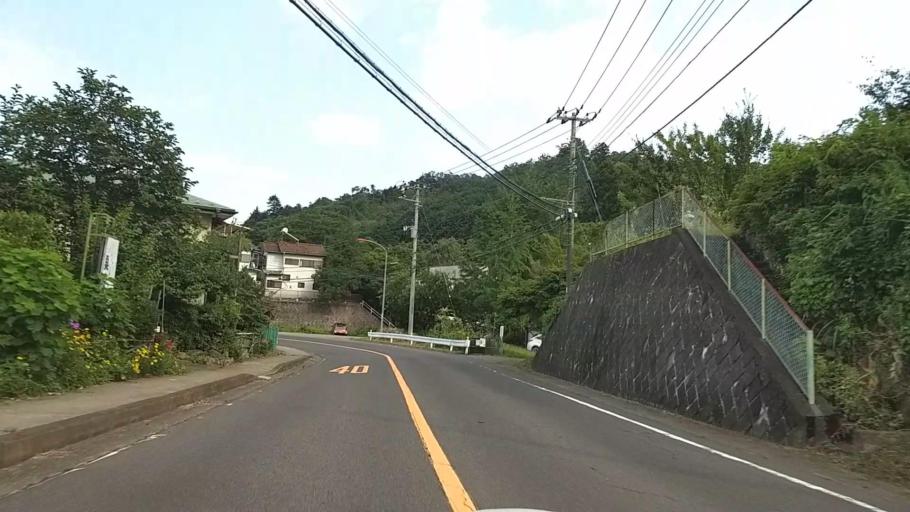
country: JP
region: Yamanashi
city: Uenohara
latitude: 35.6139
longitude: 139.1421
